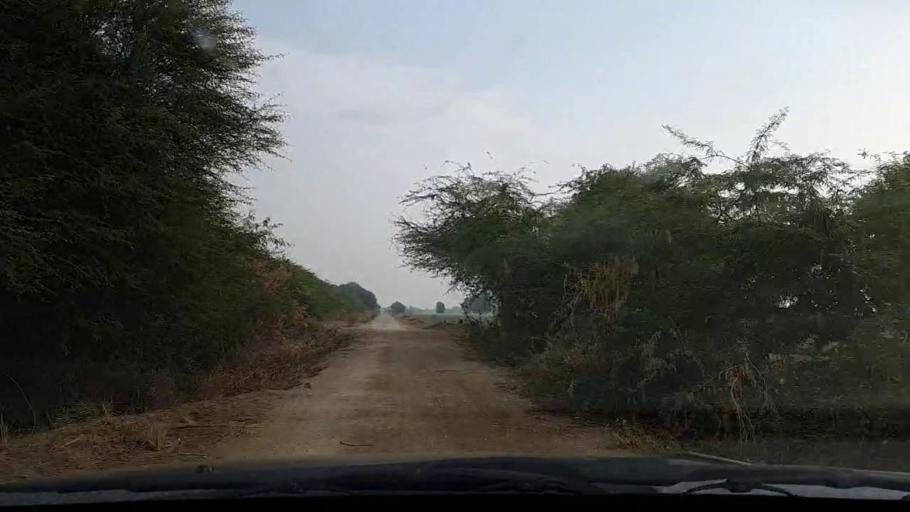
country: PK
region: Sindh
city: Pithoro
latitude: 25.7075
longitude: 69.3854
